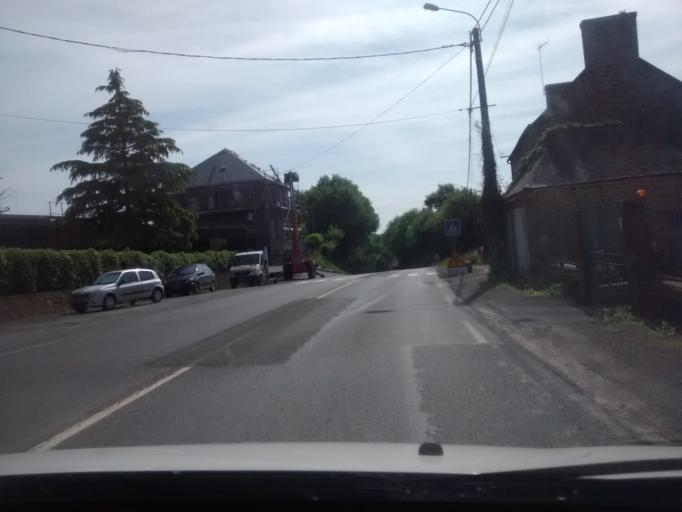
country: FR
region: Brittany
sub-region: Departement d'Ille-et-Vilaine
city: Romagne
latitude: 48.3505
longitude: -1.2456
